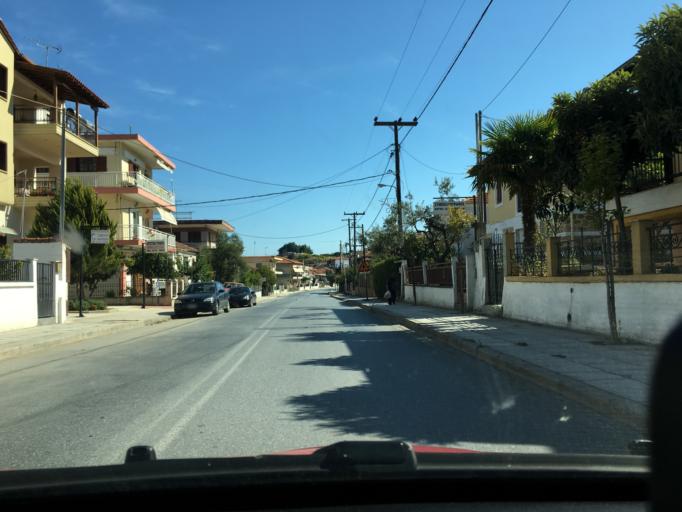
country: GR
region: Central Macedonia
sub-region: Nomos Chalkidikis
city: Ierissos
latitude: 40.3966
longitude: 23.8788
